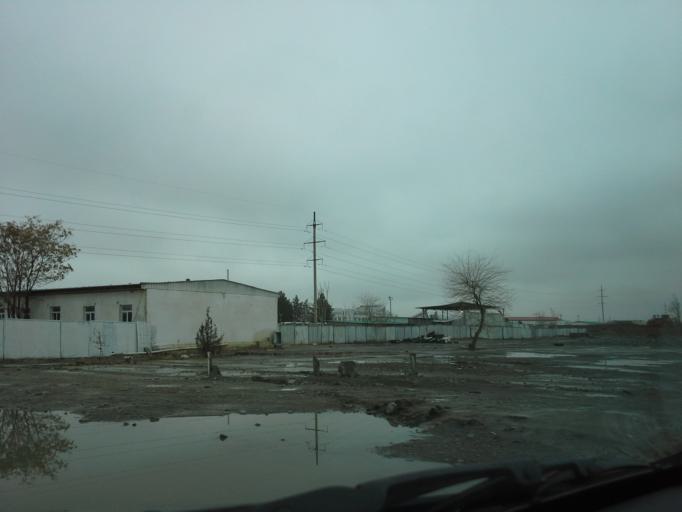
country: TM
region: Ahal
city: Ashgabat
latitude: 37.9512
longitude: 58.4243
